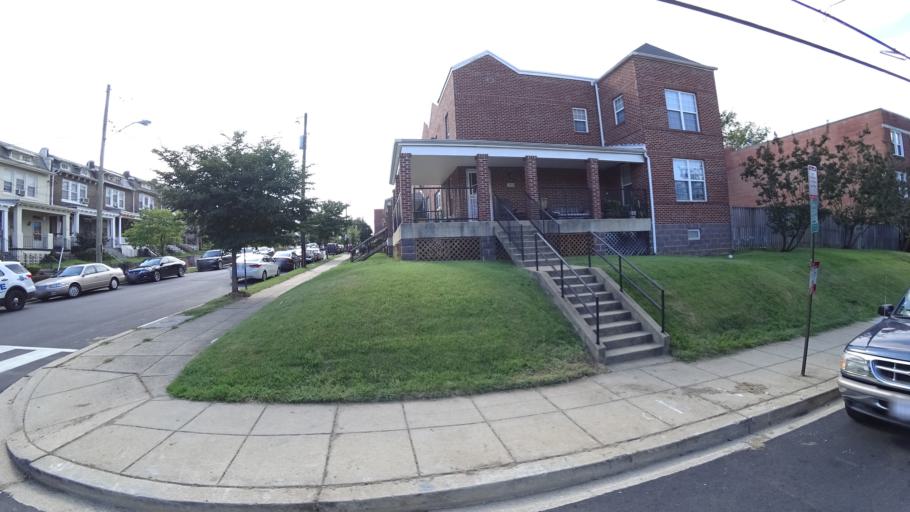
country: US
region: Maryland
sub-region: Prince George's County
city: Mount Rainier
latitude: 38.9266
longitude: -76.9962
